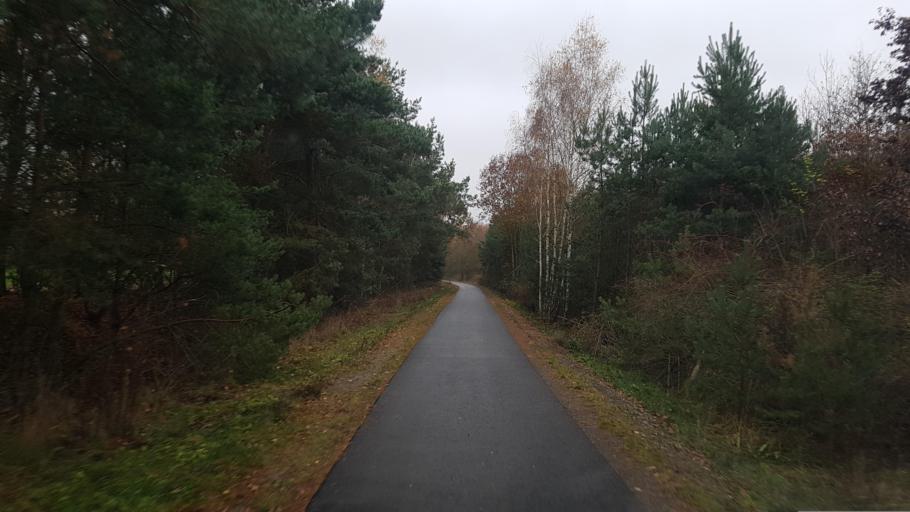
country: DE
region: Brandenburg
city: Crinitz
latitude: 51.7590
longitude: 13.7916
